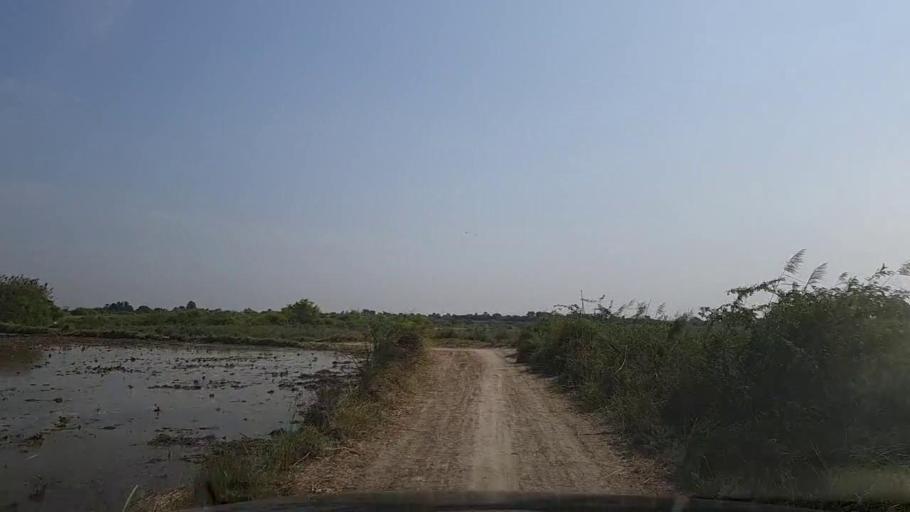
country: PK
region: Sindh
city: Thatta
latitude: 24.8036
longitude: 67.8677
